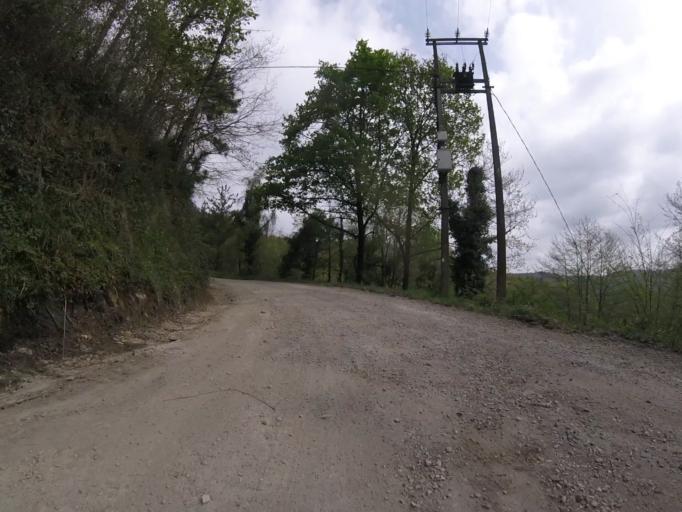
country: ES
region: Basque Country
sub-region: Provincia de Guipuzcoa
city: Asteasu
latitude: 43.2216
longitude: -2.0943
